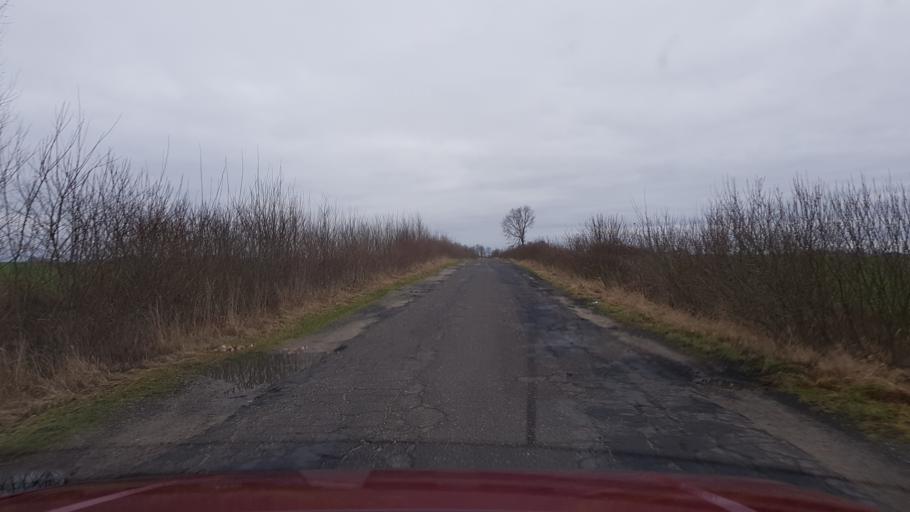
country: PL
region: West Pomeranian Voivodeship
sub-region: Powiat koszalinski
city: Mielno
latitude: 54.1542
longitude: 16.0324
